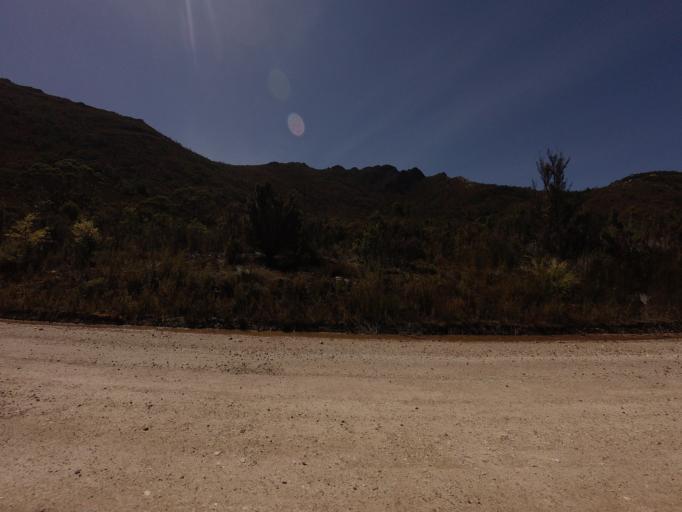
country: AU
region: Tasmania
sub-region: Huon Valley
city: Geeveston
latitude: -42.9358
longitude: 146.3471
